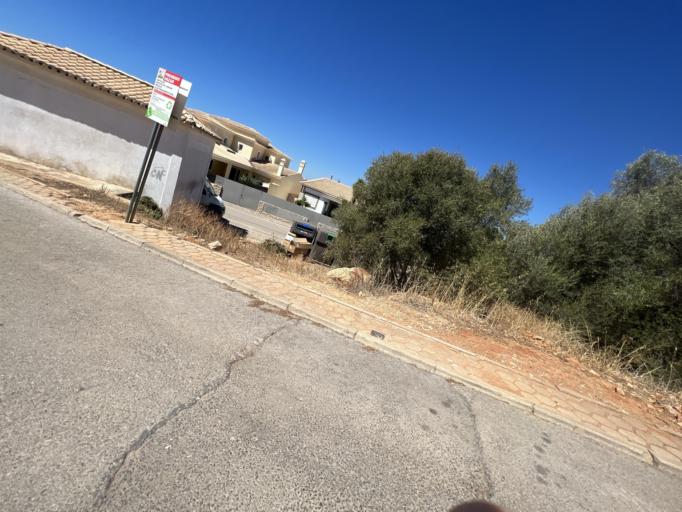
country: PT
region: Faro
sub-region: Portimao
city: Portimao
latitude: 37.1298
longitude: -8.5193
